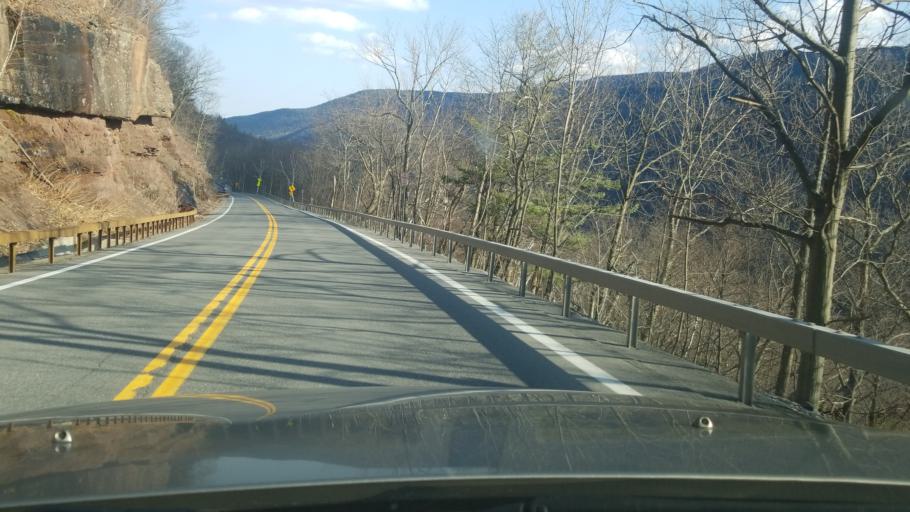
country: US
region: New York
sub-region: Greene County
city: Palenville
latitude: 42.1915
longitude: -74.0774
